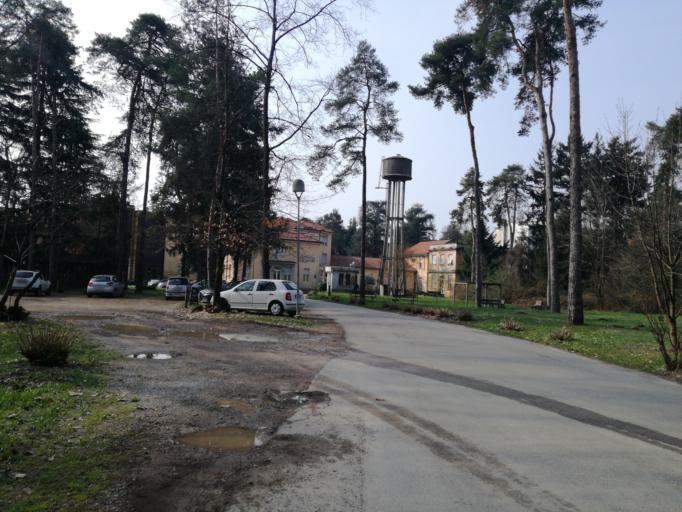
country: IT
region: Lombardy
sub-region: Provincia di Monza e Brianza
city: Ornago
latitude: 45.5932
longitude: 9.4319
